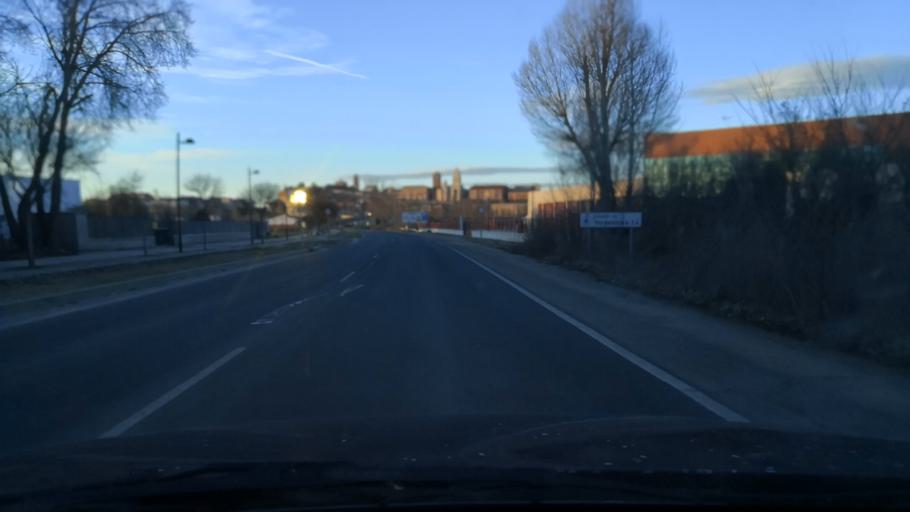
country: ES
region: Castille and Leon
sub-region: Provincia de Valladolid
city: Tordesillas
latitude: 41.4934
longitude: -4.9982
